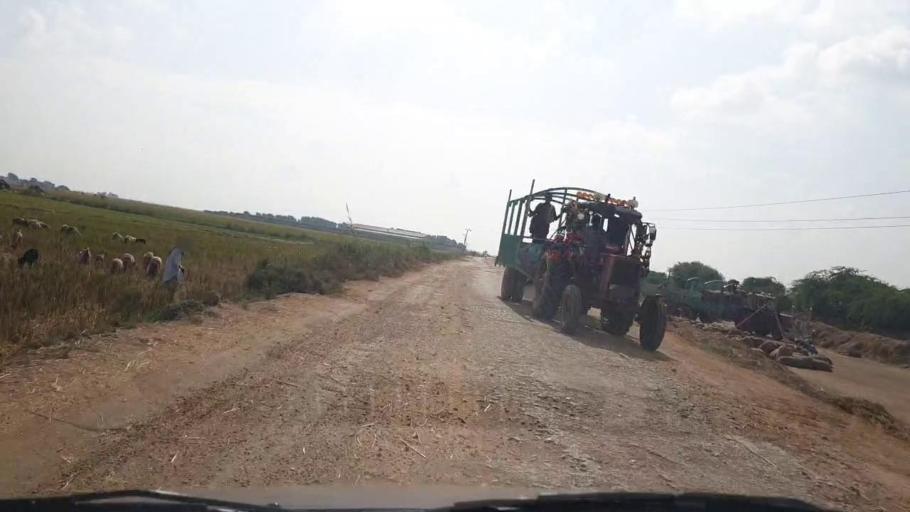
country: PK
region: Sindh
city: Kario
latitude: 24.6410
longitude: 68.5454
